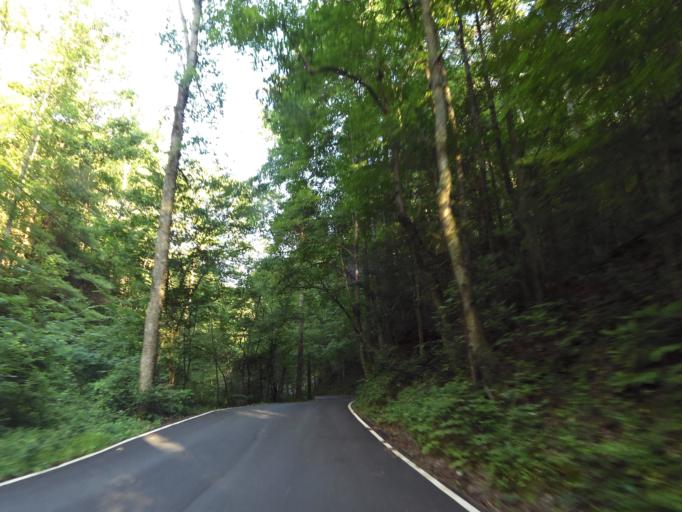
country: US
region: Tennessee
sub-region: Blount County
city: Maryville
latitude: 35.6929
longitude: -83.8967
